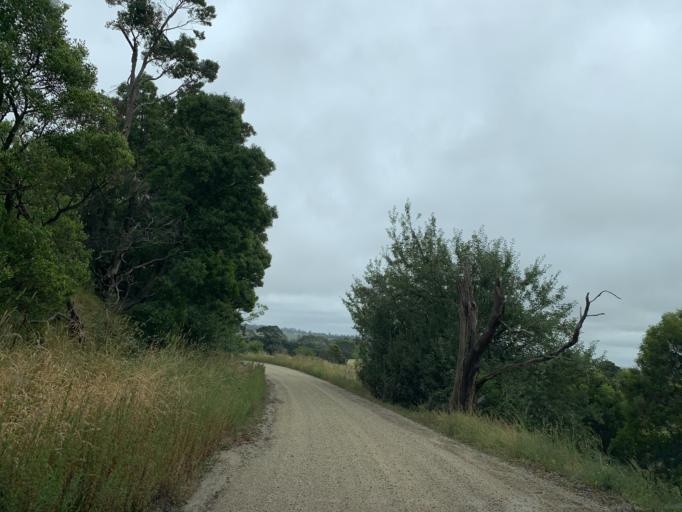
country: AU
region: Victoria
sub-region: Baw Baw
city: Warragul
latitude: -38.3477
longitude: 145.8678
